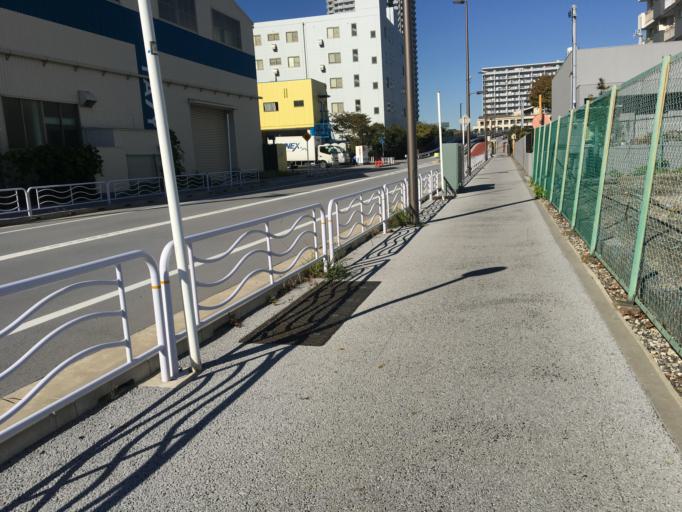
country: JP
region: Tokyo
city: Urayasu
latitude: 35.6529
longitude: 139.8159
